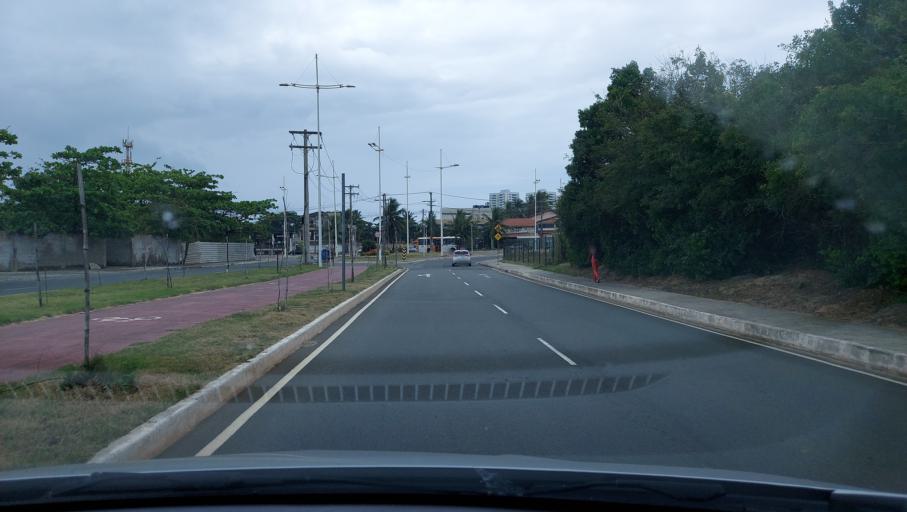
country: BR
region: Bahia
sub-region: Lauro De Freitas
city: Lauro de Freitas
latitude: -12.9614
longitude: -38.4030
